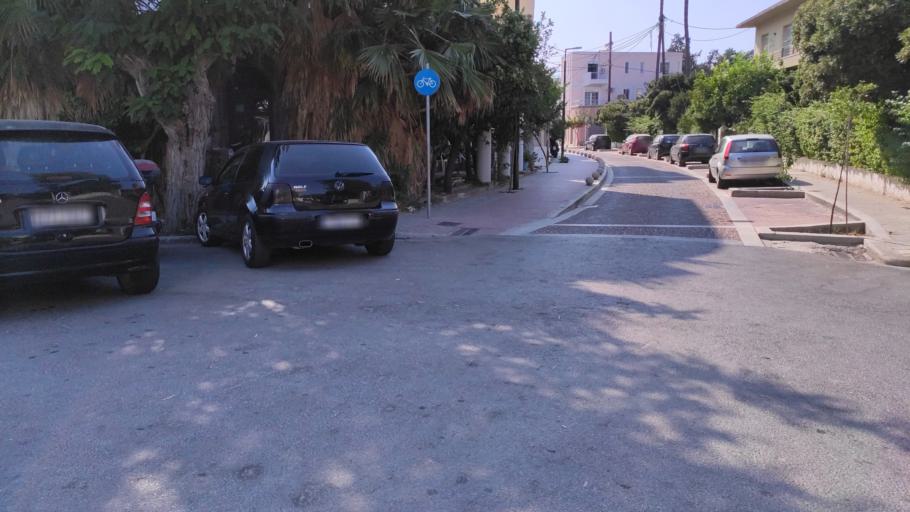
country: GR
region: South Aegean
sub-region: Nomos Dodekanisou
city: Kos
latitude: 36.8913
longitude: 27.2920
